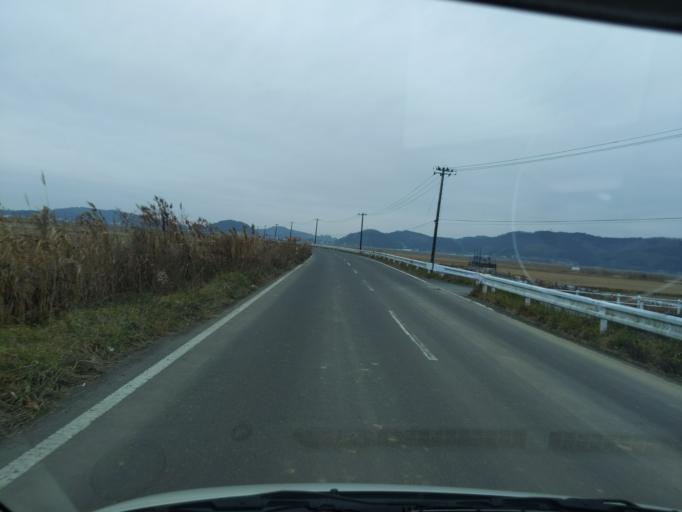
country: JP
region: Iwate
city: Ichinoseki
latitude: 38.7465
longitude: 141.2496
